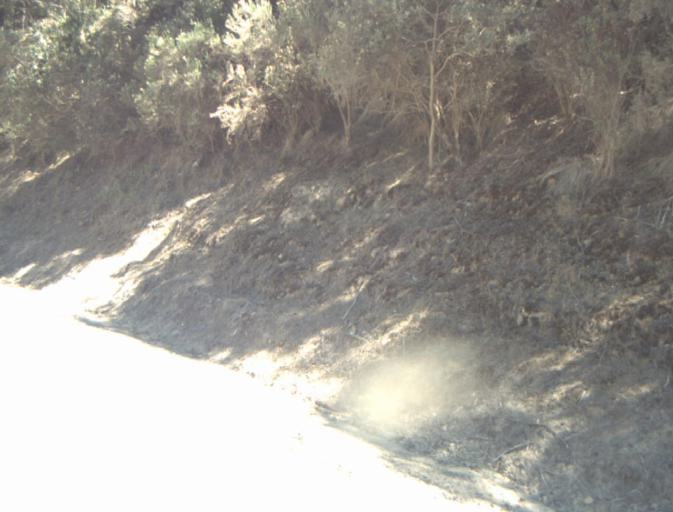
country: AU
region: Tasmania
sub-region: Dorset
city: Scottsdale
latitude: -41.3218
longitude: 147.4146
